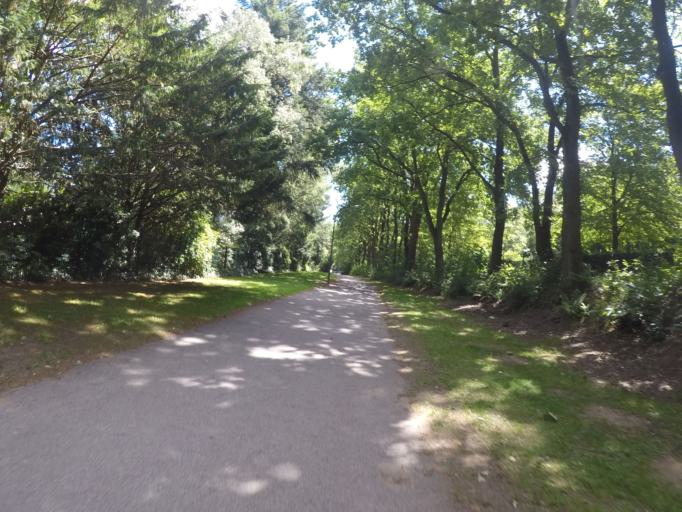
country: DE
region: Schleswig-Holstein
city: Halstenbek
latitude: 53.5741
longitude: 9.7999
